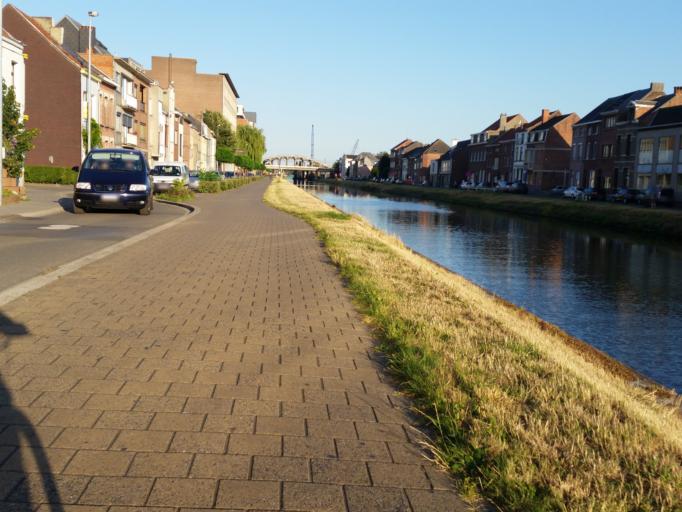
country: BE
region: Flanders
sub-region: Provincie Antwerpen
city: Mechelen
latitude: 51.0191
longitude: 4.4755
